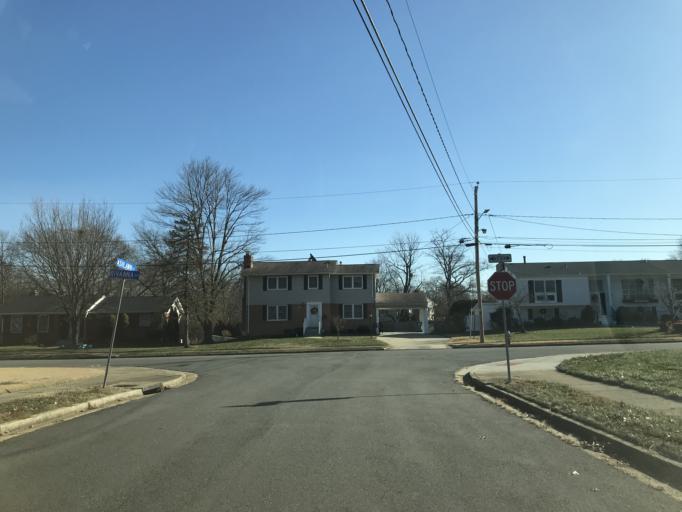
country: US
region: Virginia
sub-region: Fairfax County
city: Springfield
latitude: 38.7850
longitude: -77.1695
